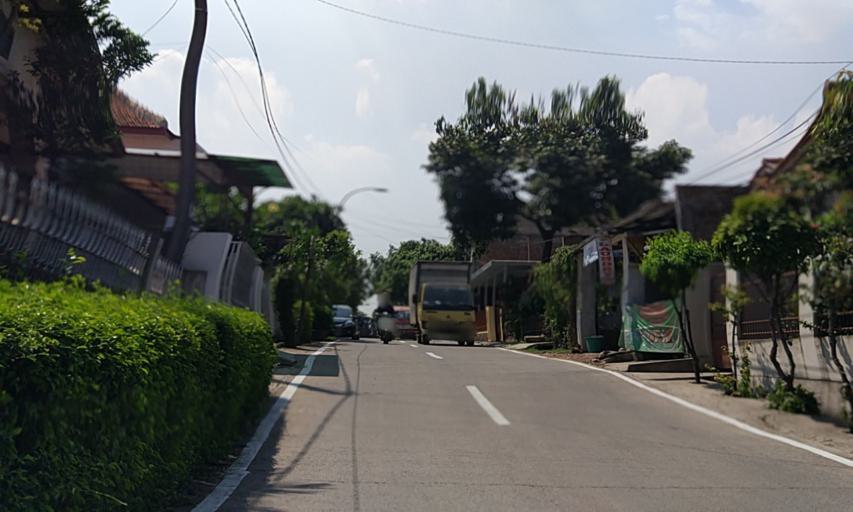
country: ID
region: West Java
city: Cimahi
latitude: -6.9199
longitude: 107.5562
